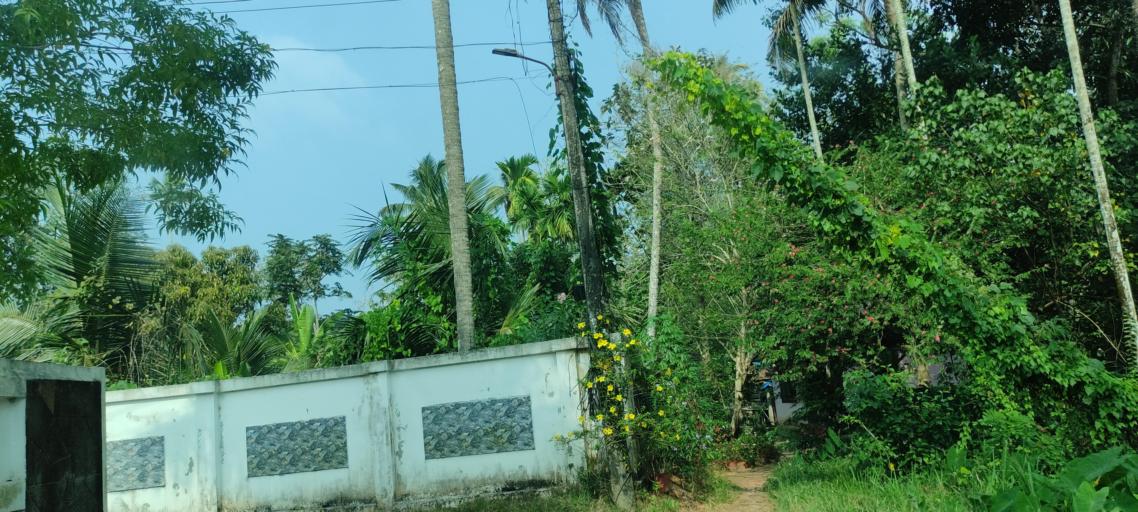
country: IN
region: Kerala
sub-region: Alappuzha
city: Shertallai
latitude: 9.6795
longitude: 76.3384
